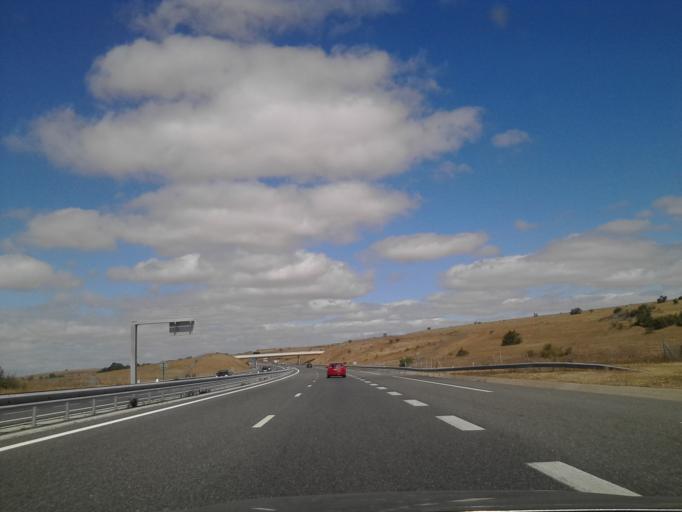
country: FR
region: Midi-Pyrenees
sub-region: Departement de l'Aveyron
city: La Cavalerie
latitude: 44.0145
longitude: 3.1374
